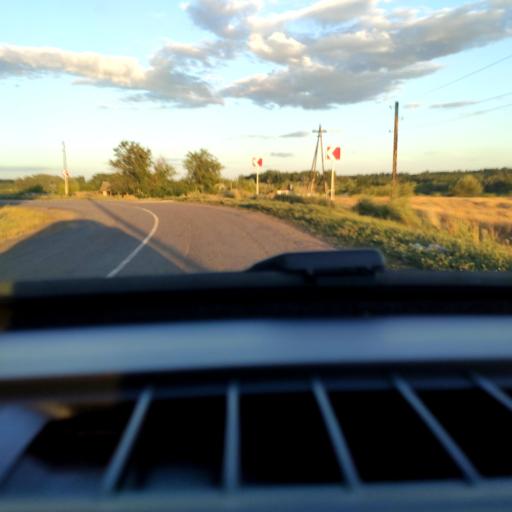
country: RU
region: Voronezj
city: Orlovo
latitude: 51.6155
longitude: 39.7942
